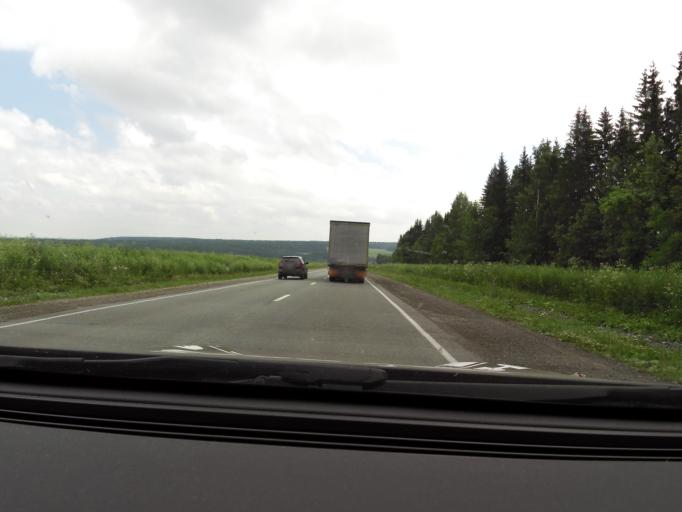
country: RU
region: Perm
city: Suksun
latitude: 57.0727
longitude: 57.4142
